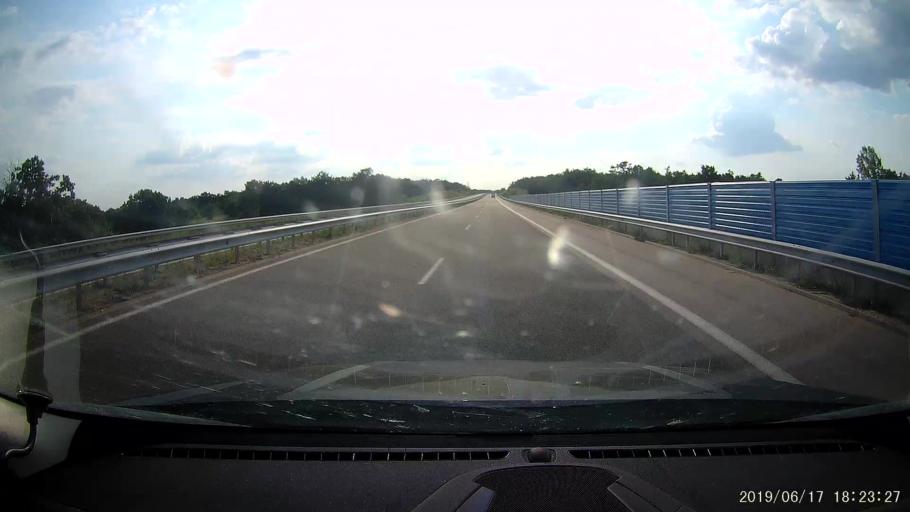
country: BG
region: Khaskovo
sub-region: Obshtina Simeonovgrad
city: Simeonovgrad
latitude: 41.9756
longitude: 25.7210
